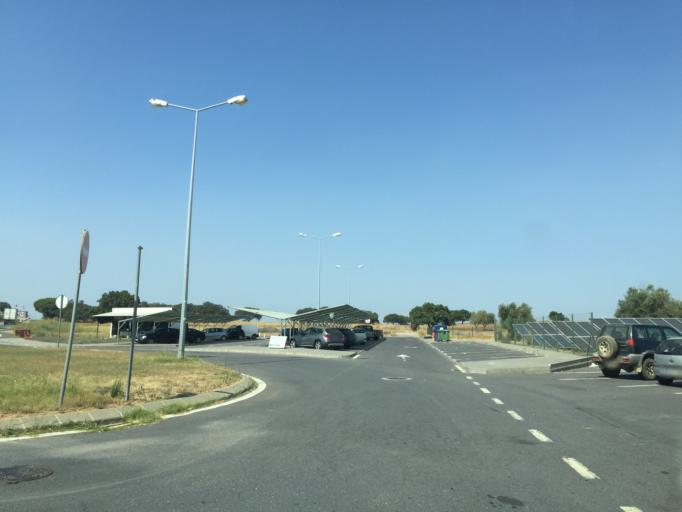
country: PT
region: Beja
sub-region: Aljustrel
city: Aljustrel
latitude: 37.9490
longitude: -8.3807
